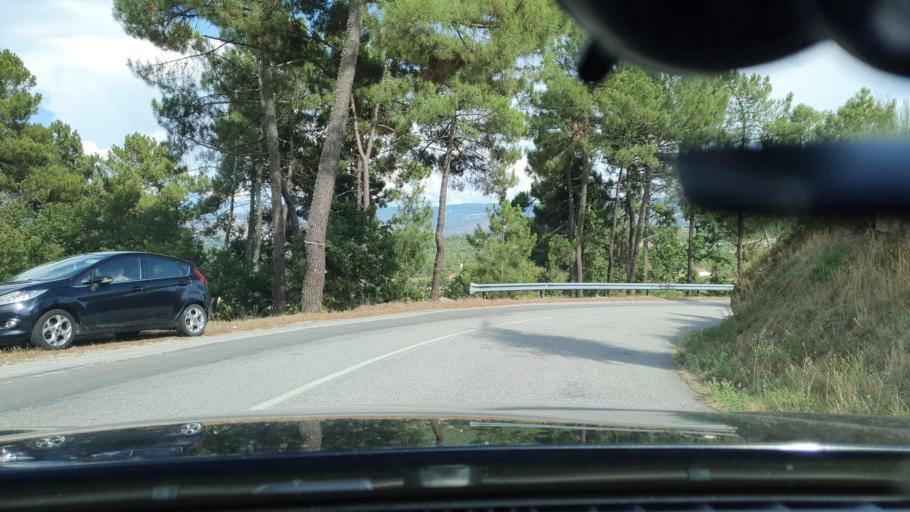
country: PT
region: Vila Real
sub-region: Chaves
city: Chaves
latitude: 41.7823
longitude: -7.4947
